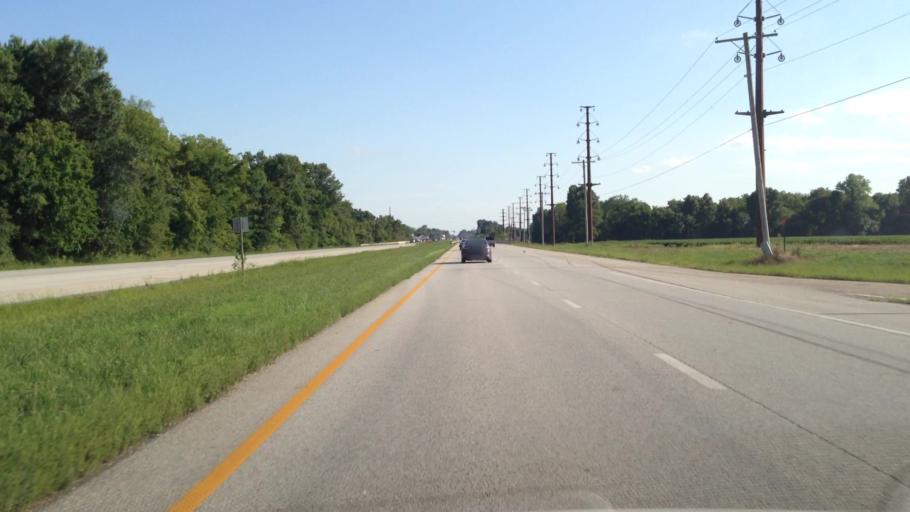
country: US
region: Kansas
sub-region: Crawford County
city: Frontenac
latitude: 37.4768
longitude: -94.7053
